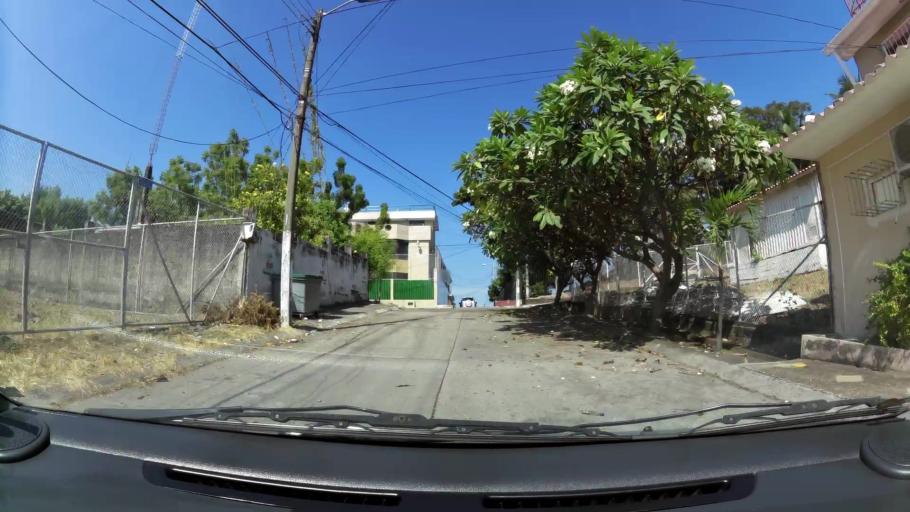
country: EC
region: Guayas
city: Guayaquil
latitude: -2.1827
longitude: -79.9140
